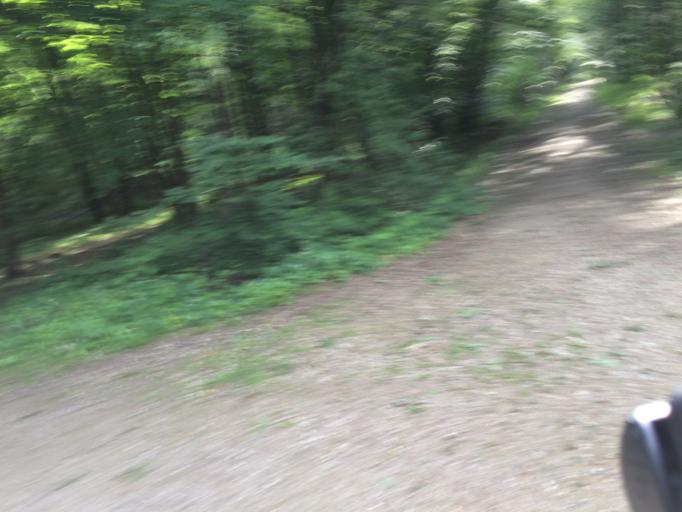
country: FR
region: Ile-de-France
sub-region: Departement de l'Essonne
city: Igny
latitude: 48.7520
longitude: 2.2410
